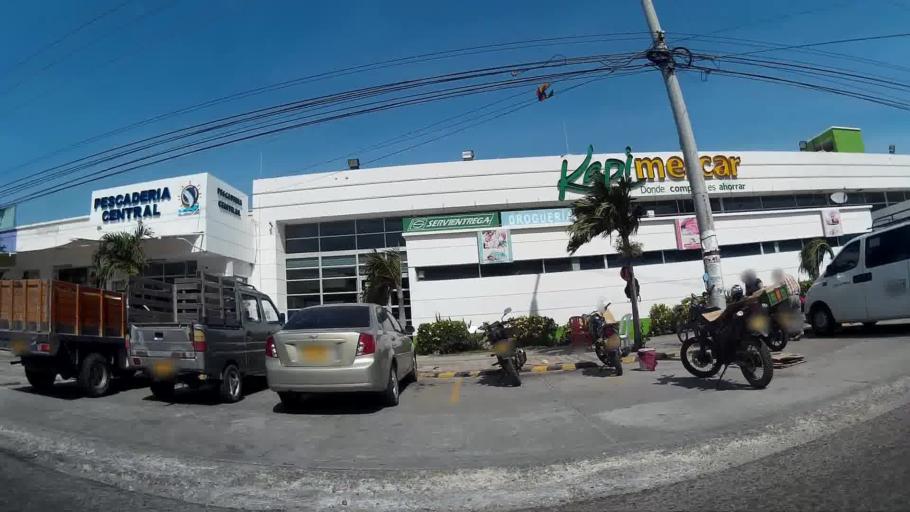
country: CO
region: Magdalena
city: Santa Marta
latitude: 11.1942
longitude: -74.2258
